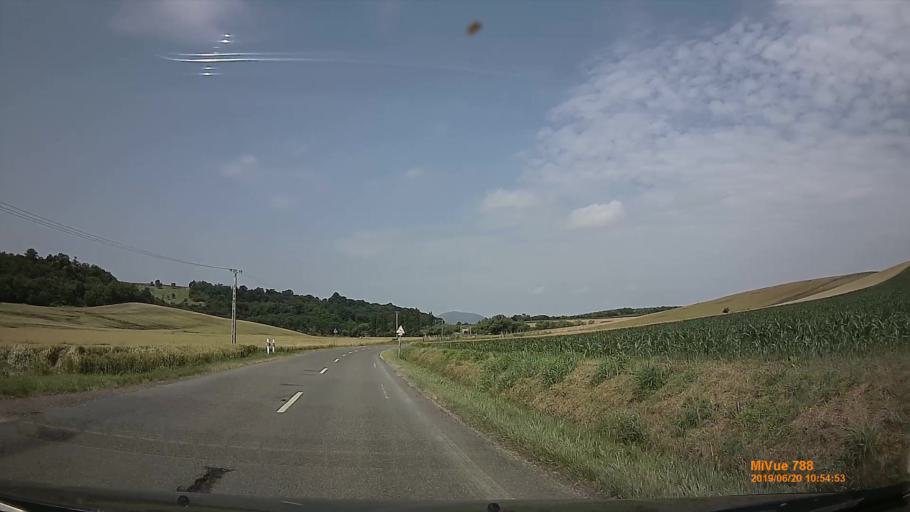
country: HU
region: Baranya
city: Mecseknadasd
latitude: 46.1535
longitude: 18.5587
